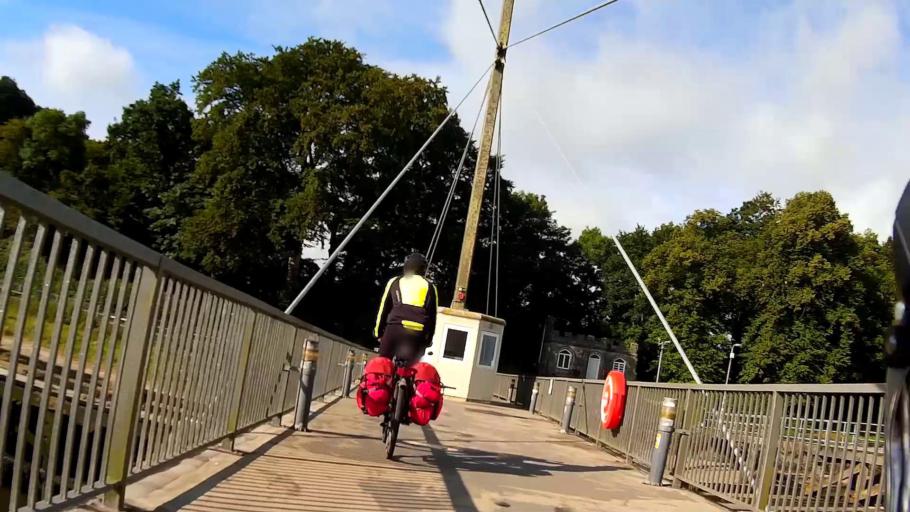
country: GB
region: Wales
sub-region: Gwynedd
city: Caernarfon
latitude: 53.1390
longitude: -4.2785
